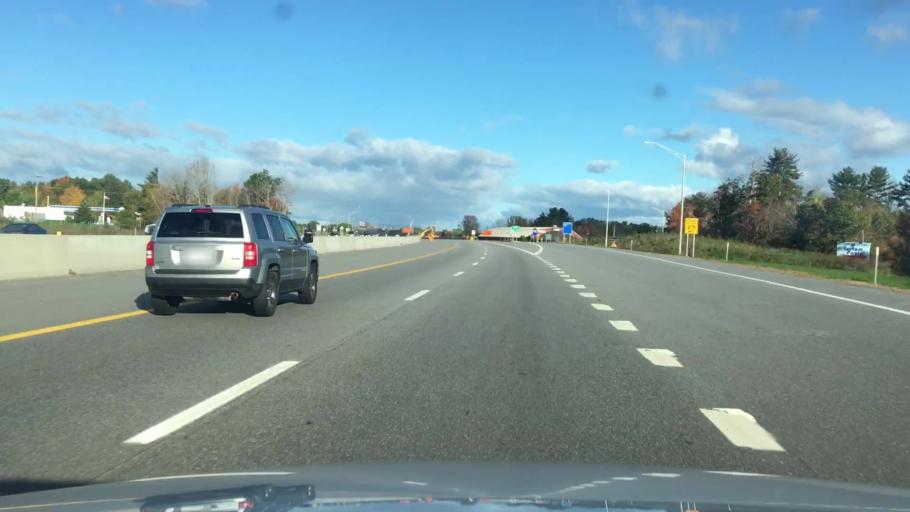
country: US
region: Maine
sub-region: York County
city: South Eliot
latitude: 43.1109
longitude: -70.8169
